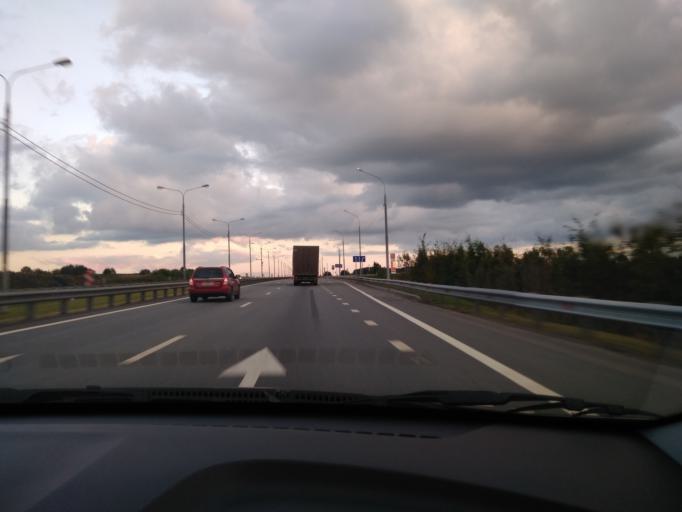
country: RU
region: Moskovskaya
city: Zhukovskiy
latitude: 55.5056
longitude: 38.1402
